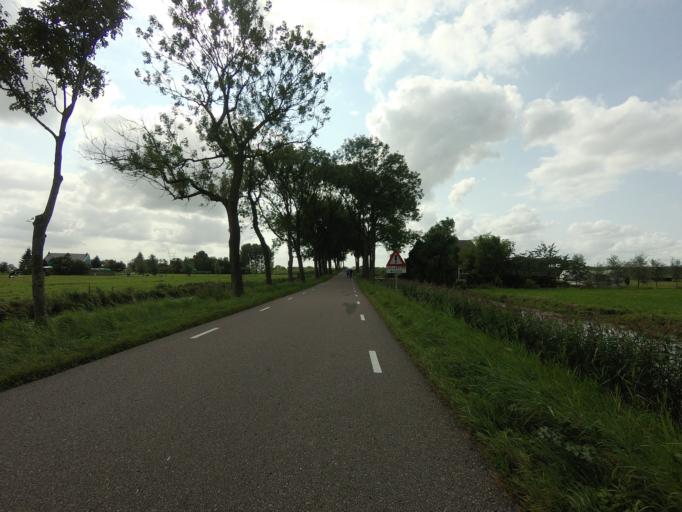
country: NL
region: North Holland
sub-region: Gemeente Purmerend
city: Purmerend
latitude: 52.4724
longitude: 4.9597
